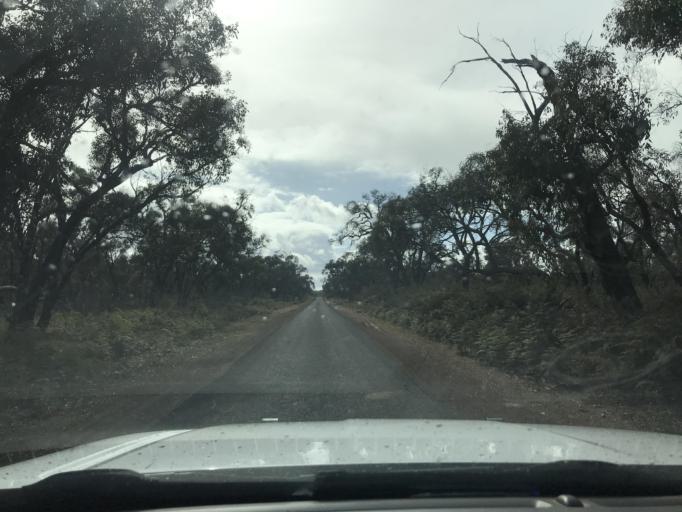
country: AU
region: South Australia
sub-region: Wattle Range
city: Penola
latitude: -37.1883
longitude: 141.2377
